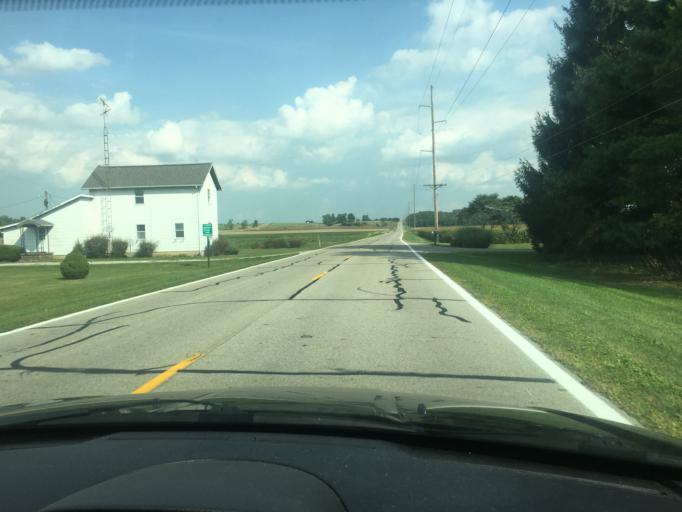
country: US
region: Ohio
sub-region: Champaign County
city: Urbana
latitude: 40.1294
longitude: -83.7980
